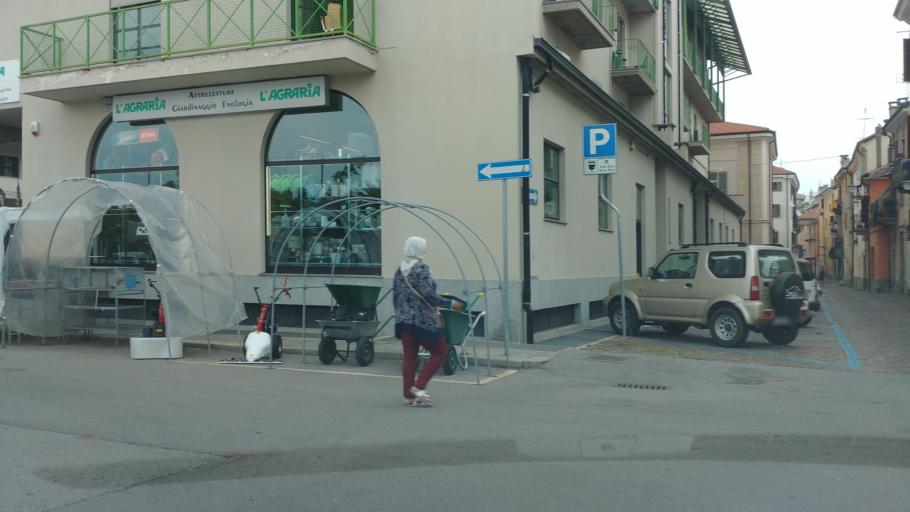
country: IT
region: Piedmont
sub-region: Provincia di Cuneo
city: Cuneo
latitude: 44.3924
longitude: 7.5474
